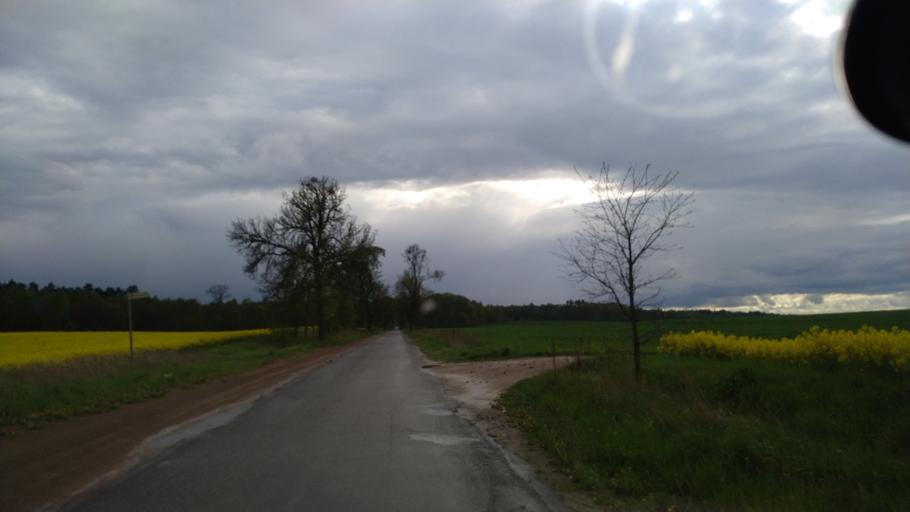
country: PL
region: Pomeranian Voivodeship
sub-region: Powiat starogardzki
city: Smetowo Graniczne
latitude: 53.7137
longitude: 18.5982
